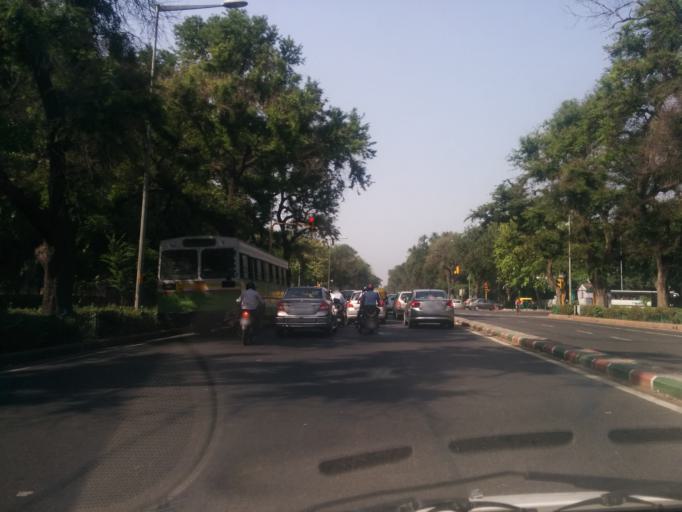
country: IN
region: NCT
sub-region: New Delhi
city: New Delhi
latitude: 28.6214
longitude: 77.2375
